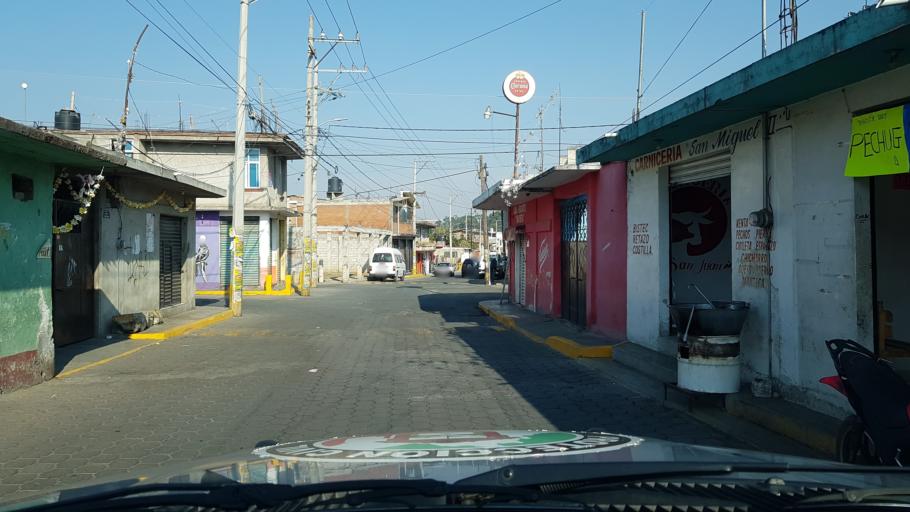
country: MX
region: Mexico
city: Ozumba de Alzate
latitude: 19.0557
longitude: -98.7721
